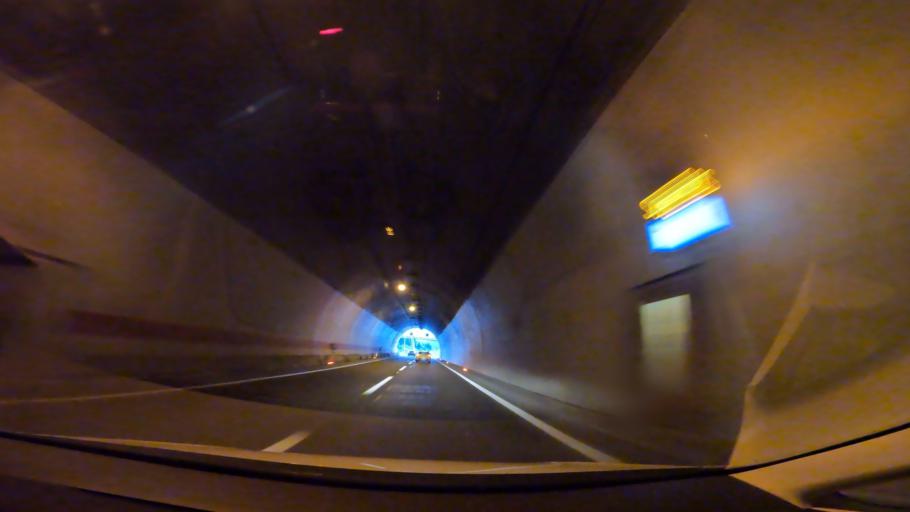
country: HR
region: Primorsko-Goranska
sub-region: Grad Delnice
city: Delnice
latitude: 45.3700
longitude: 14.7644
